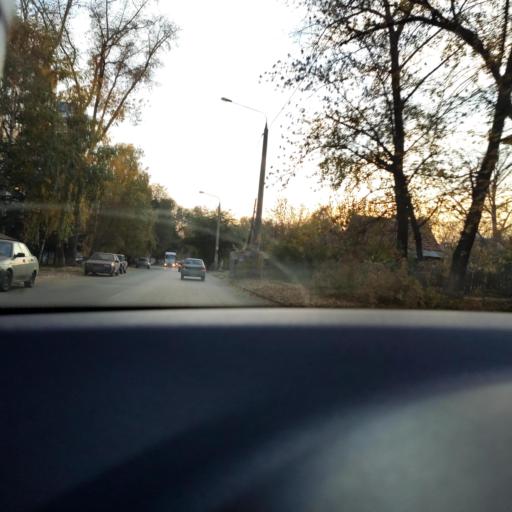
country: RU
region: Samara
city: Petra-Dubrava
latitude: 53.2318
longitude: 50.2665
